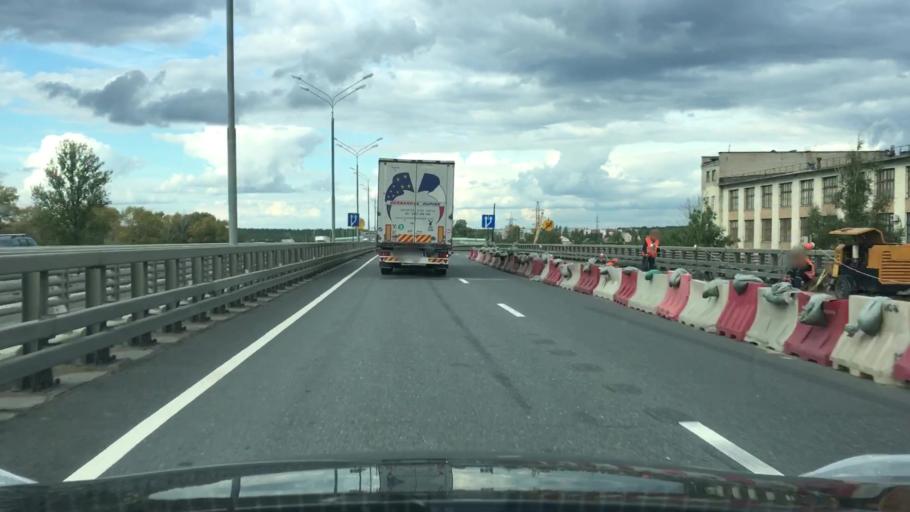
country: RU
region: Tverskaya
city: Tver
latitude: 56.8446
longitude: 35.7921
